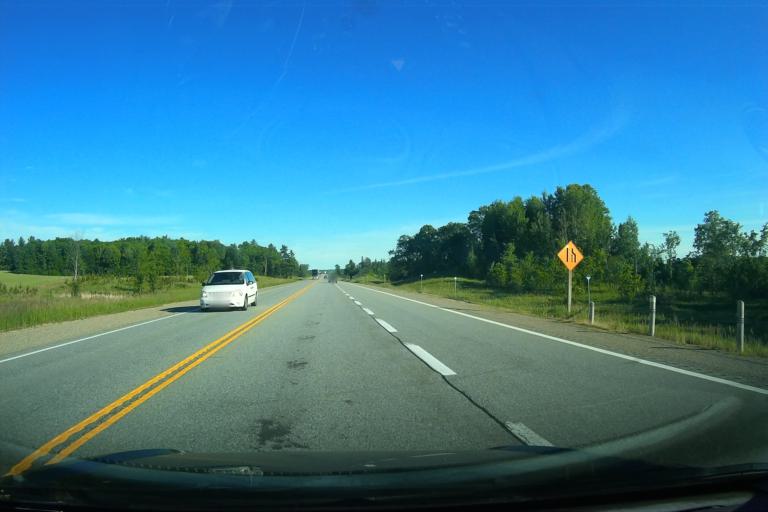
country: CA
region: Ontario
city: Renfrew
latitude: 45.5184
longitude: -76.6832
